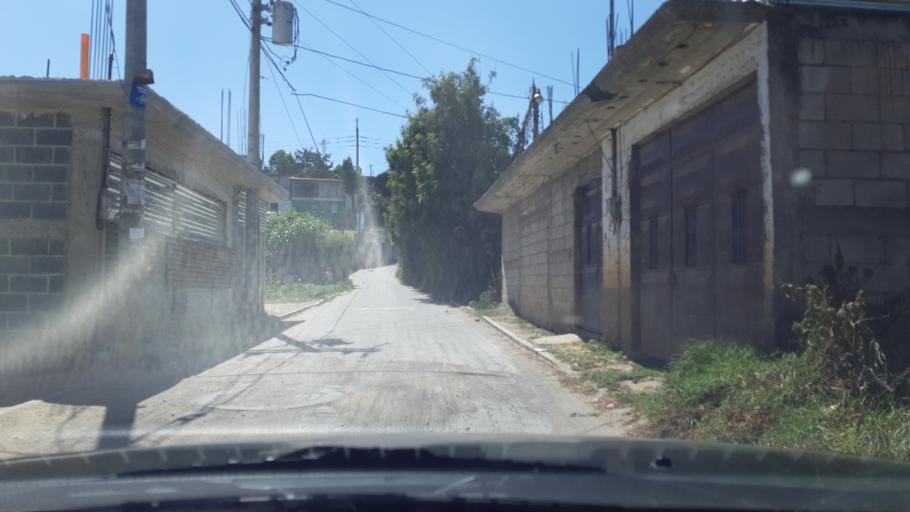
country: GT
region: Chimaltenango
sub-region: Municipio de Chimaltenango
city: Chimaltenango
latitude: 14.6691
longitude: -90.8424
